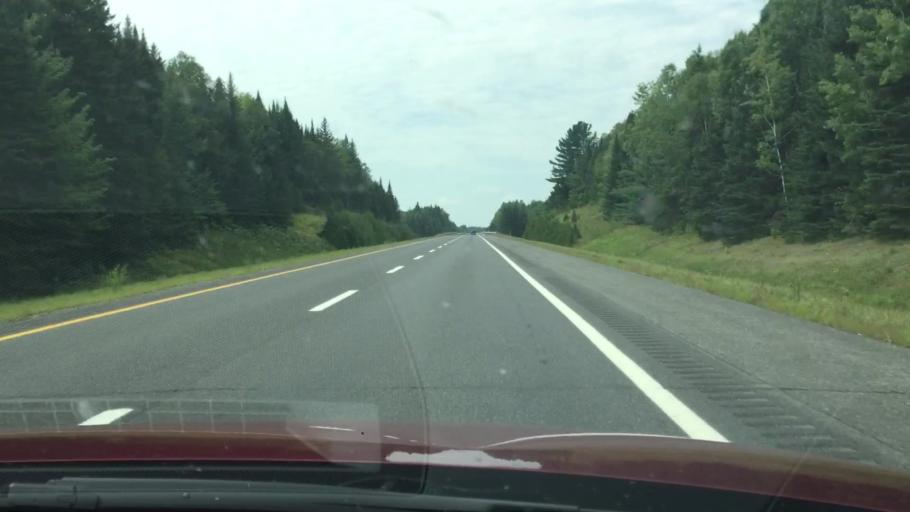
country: US
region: Maine
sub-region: Aroostook County
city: Houlton
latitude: 46.1409
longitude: -67.9920
